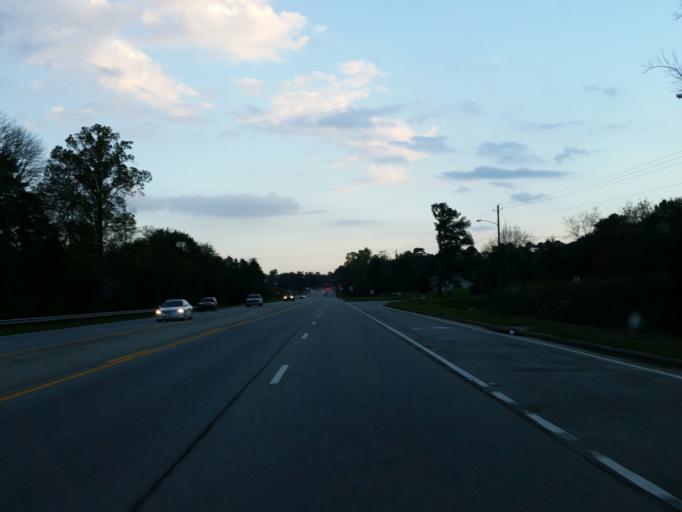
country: US
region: Georgia
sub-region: Pulaski County
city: Hawkinsville
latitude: 32.2912
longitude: -83.4820
